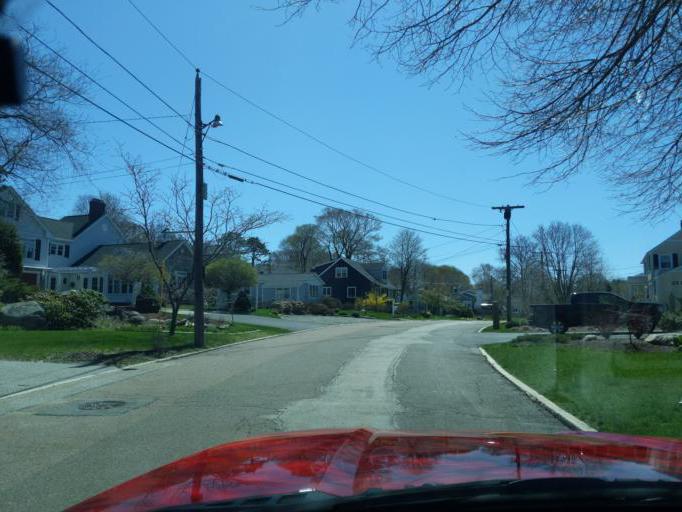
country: US
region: Massachusetts
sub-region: Essex County
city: Rockport
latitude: 42.6570
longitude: -70.6052
